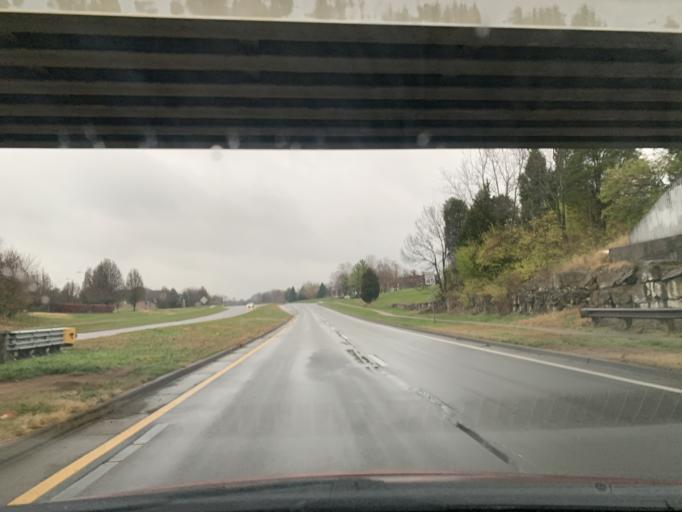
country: US
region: Kentucky
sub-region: Jefferson County
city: Hurstbourne Acres
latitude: 38.1990
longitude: -85.6029
